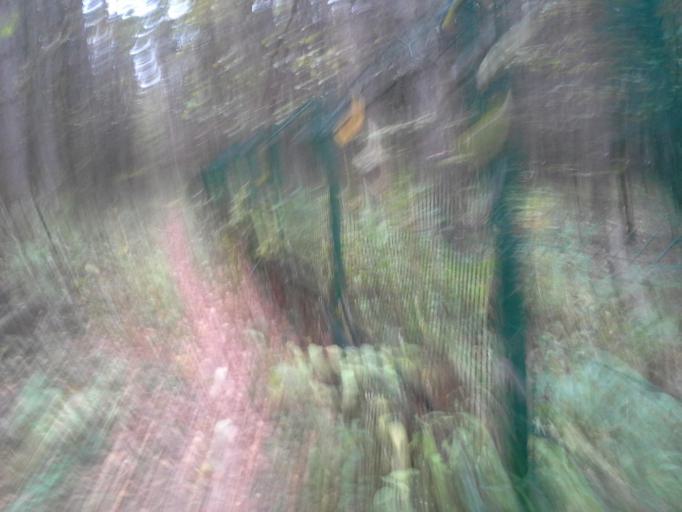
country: RU
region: Moskovskaya
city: Gorki Vtoryye
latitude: 55.6909
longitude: 37.1616
